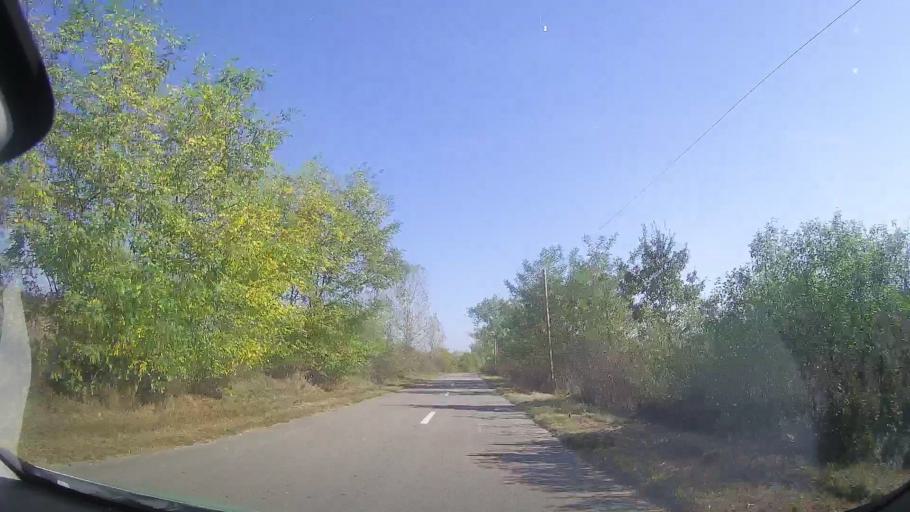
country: RO
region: Timis
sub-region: Comuna Secas
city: Secas
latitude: 45.8533
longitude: 21.7961
